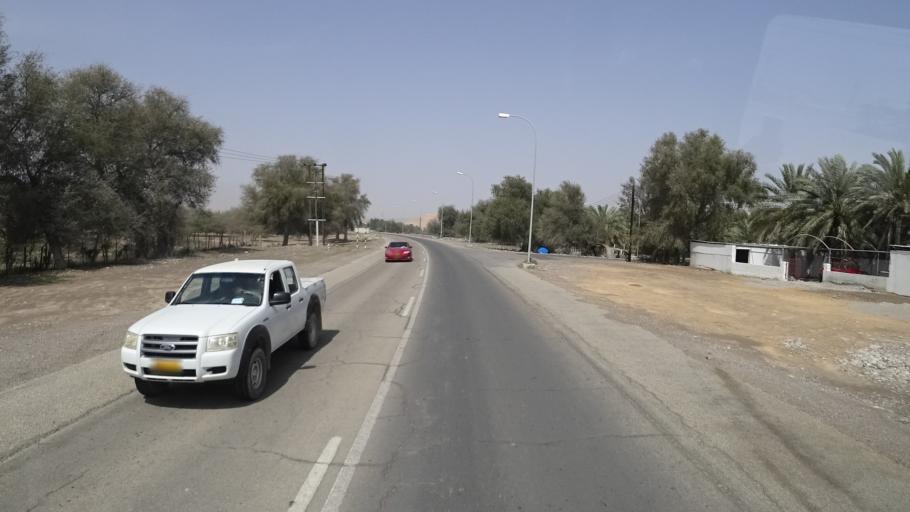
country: OM
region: Muhafazat Masqat
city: Muscat
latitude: 23.2065
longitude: 58.9639
